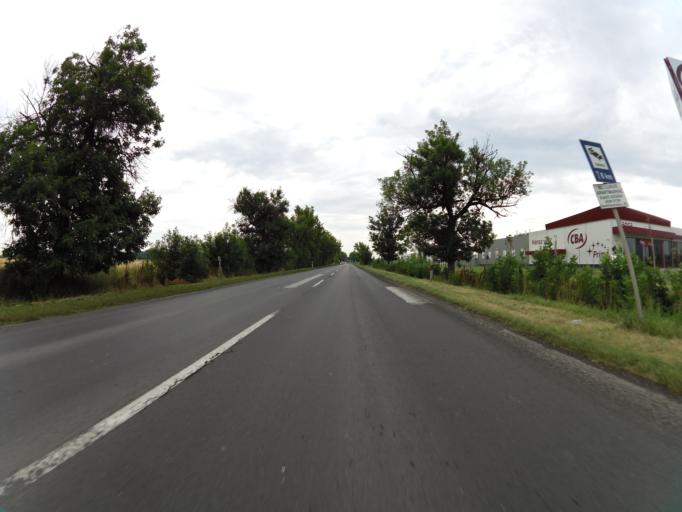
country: HU
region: Csongrad
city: Szeged
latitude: 46.2879
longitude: 20.0876
